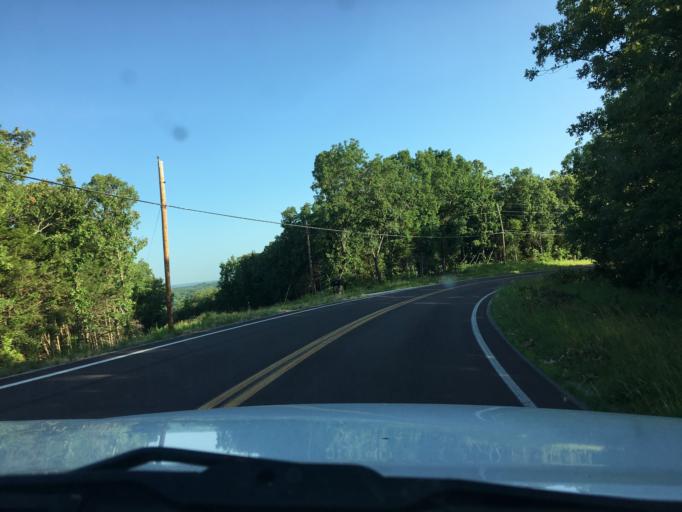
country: US
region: Missouri
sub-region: Gasconade County
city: Owensville
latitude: 38.4494
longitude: -91.6341
